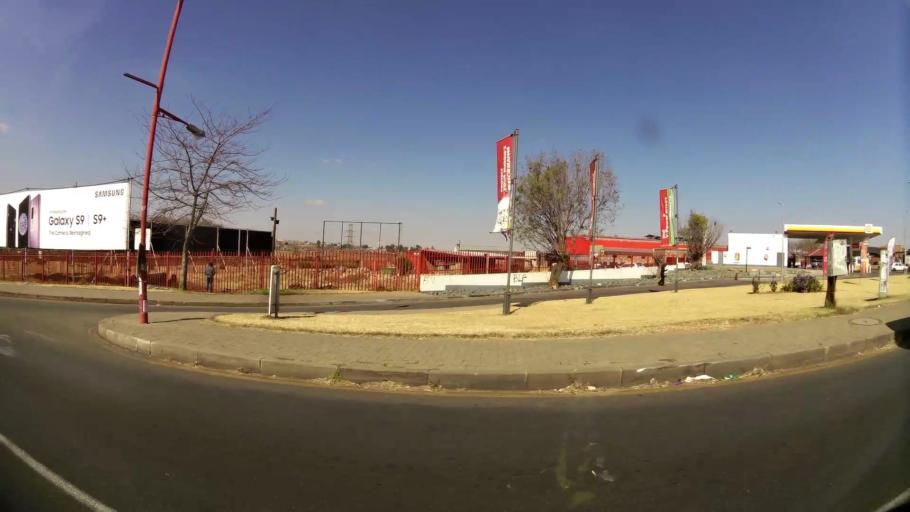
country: ZA
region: Gauteng
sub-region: City of Johannesburg Metropolitan Municipality
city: Soweto
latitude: -26.2649
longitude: 27.8794
